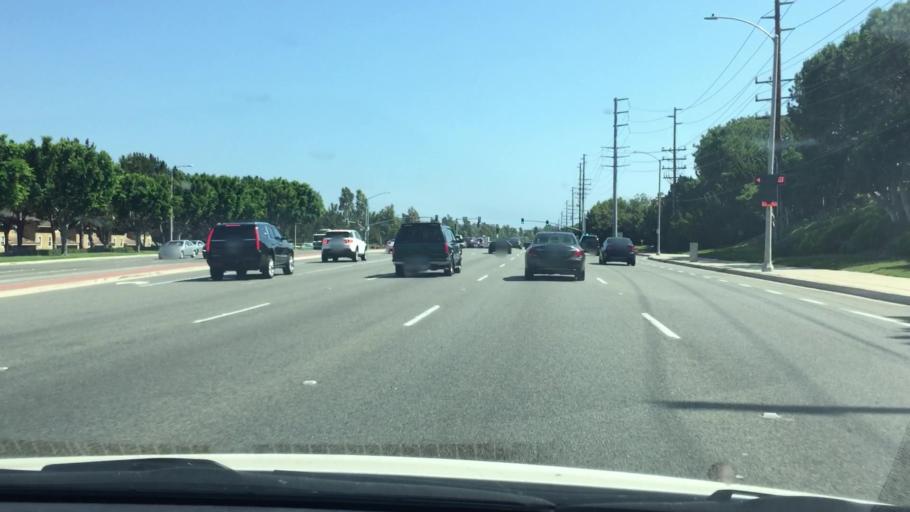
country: US
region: California
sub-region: Orange County
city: San Joaquin Hills
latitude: 33.6311
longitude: -117.8632
